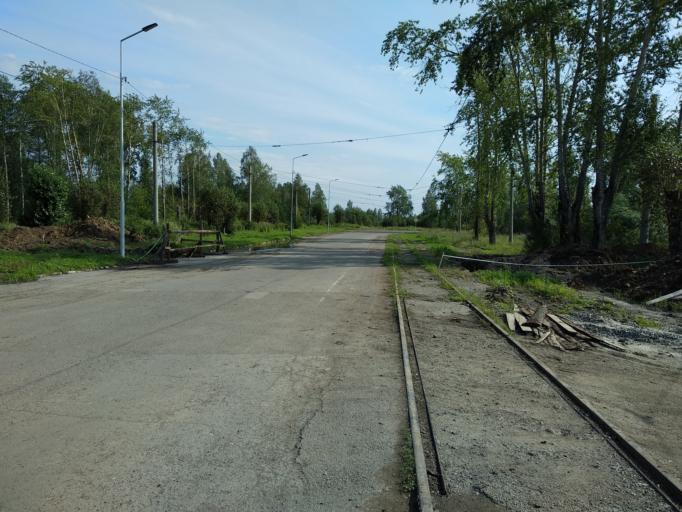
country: RU
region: Sverdlovsk
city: Volchansk
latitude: 59.8945
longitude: 60.0202
